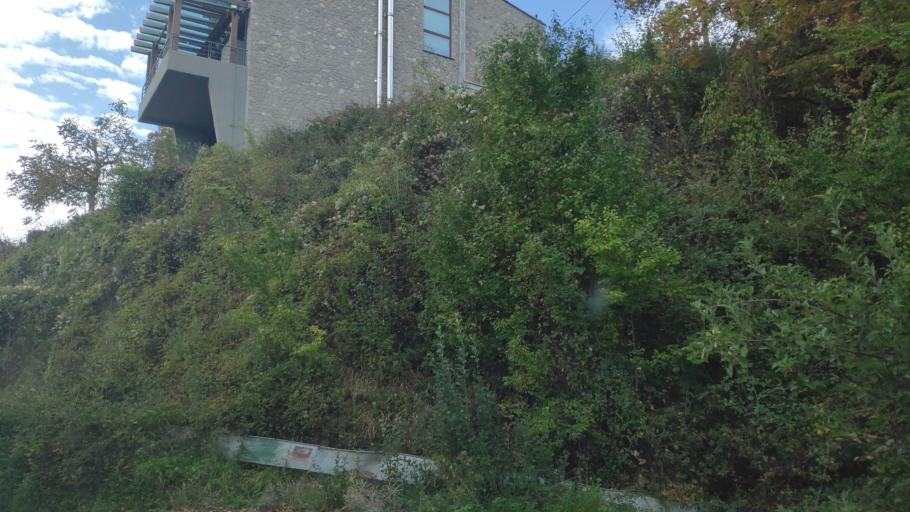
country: GR
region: Central Greece
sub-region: Nomos Fthiotidos
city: Stavros
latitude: 38.7414
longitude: 22.3368
